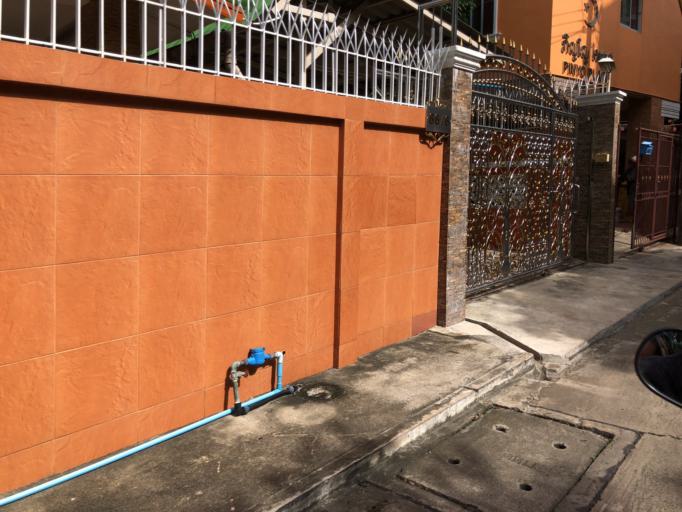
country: TH
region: Bangkok
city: Phra Khanong
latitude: 13.7194
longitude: 100.6002
